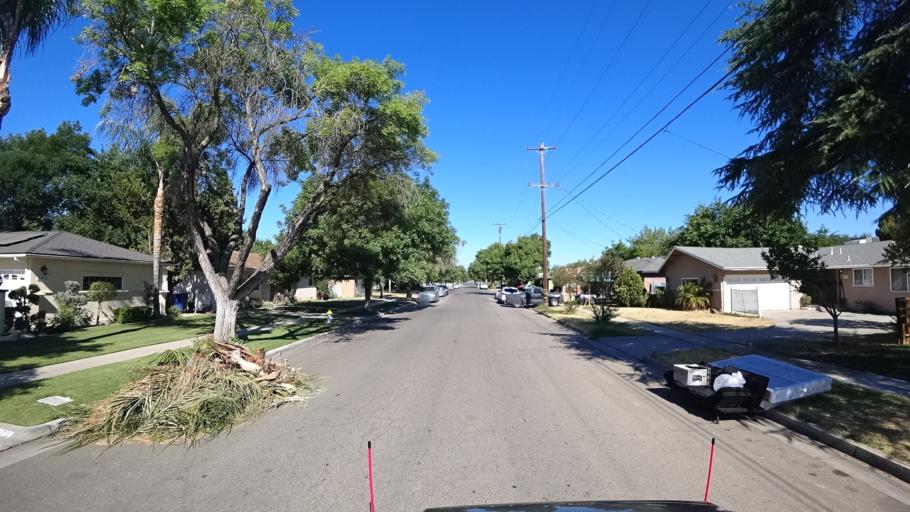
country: US
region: California
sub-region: Fresno County
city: Fresno
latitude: 36.7772
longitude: -119.7661
